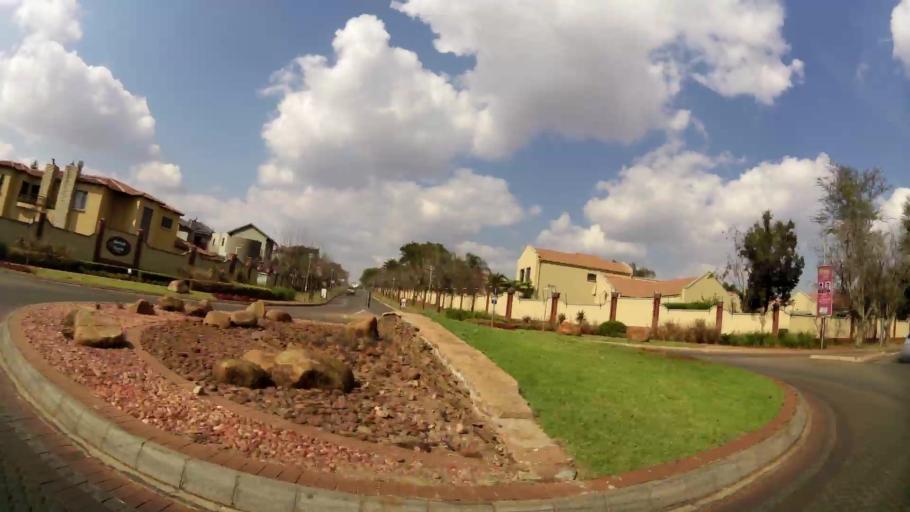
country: ZA
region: Gauteng
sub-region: City of Tshwane Metropolitan Municipality
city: Pretoria
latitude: -25.8017
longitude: 28.3315
